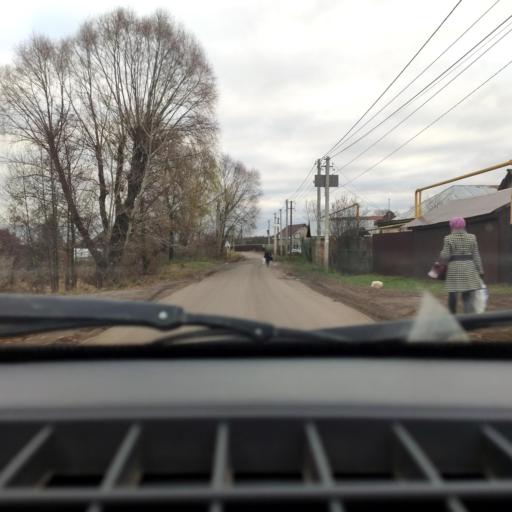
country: RU
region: Bashkortostan
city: Avdon
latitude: 54.6496
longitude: 55.7763
